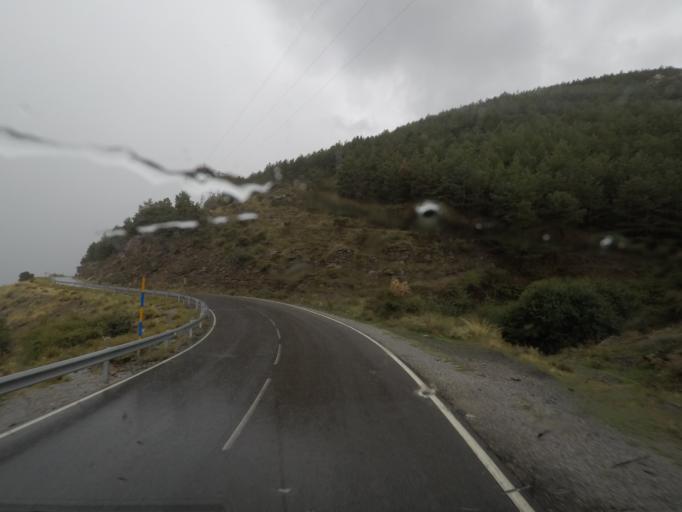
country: ES
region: Andalusia
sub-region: Provincia de Almeria
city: Bayarcal
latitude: 37.0659
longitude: -3.0174
